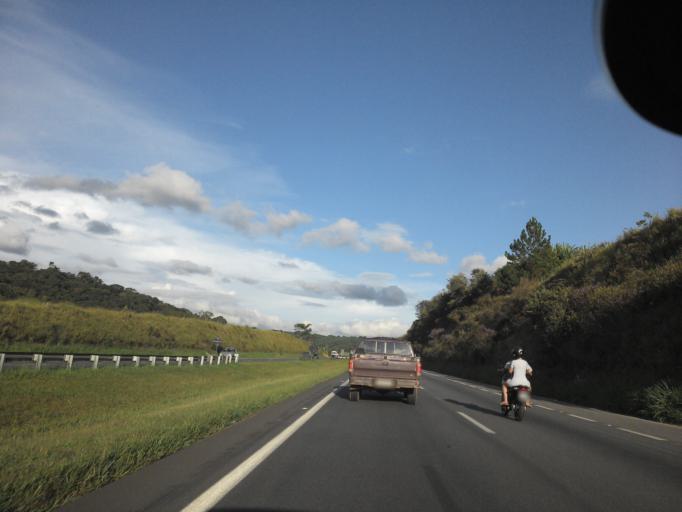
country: BR
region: Sao Paulo
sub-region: Jarinu
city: Jarinu
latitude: -23.0292
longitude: -46.7464
